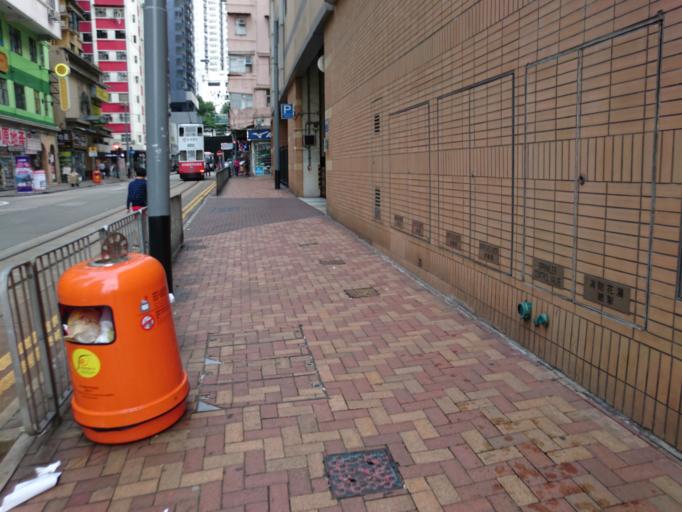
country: HK
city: Hong Kong
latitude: 22.2830
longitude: 114.1266
